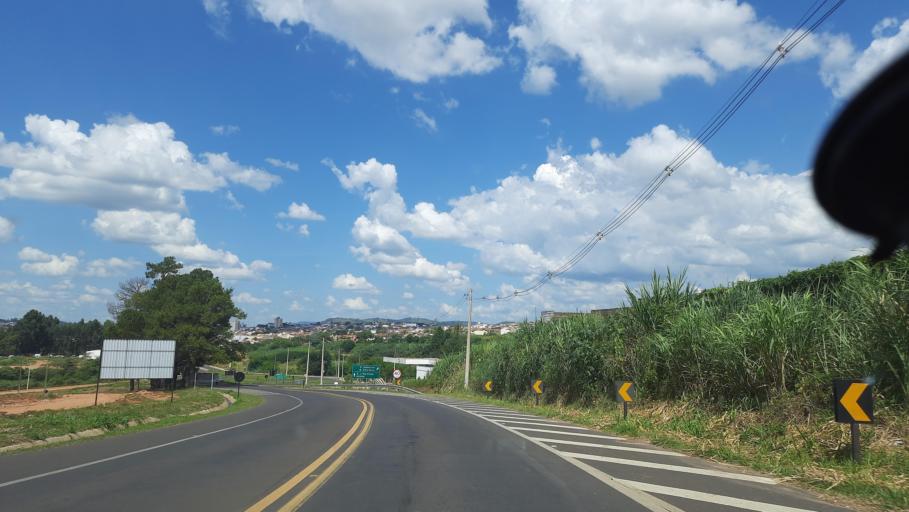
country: BR
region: Sao Paulo
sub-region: Sao Jose Do Rio Pardo
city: Sao Jose do Rio Pardo
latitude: -21.6037
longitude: -46.9178
